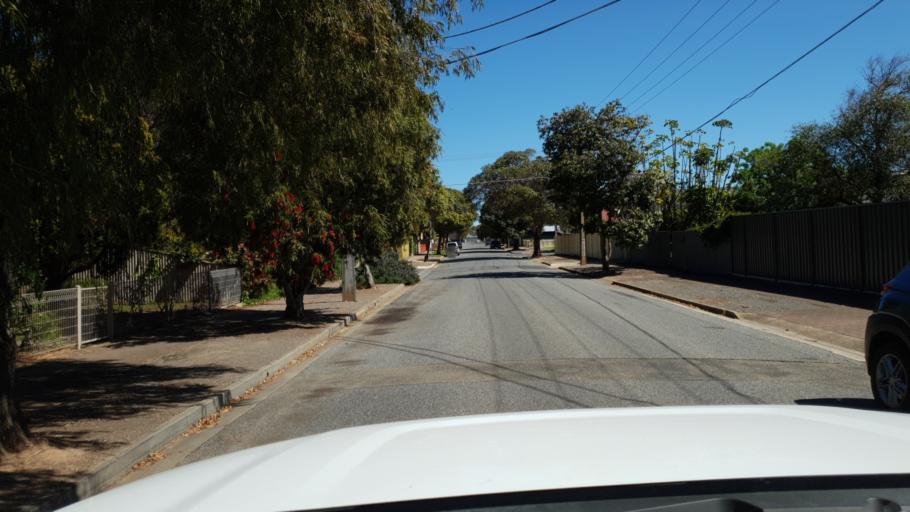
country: AU
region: South Australia
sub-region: Holdfast Bay
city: Seacliff Park
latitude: -35.0264
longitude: 138.5281
